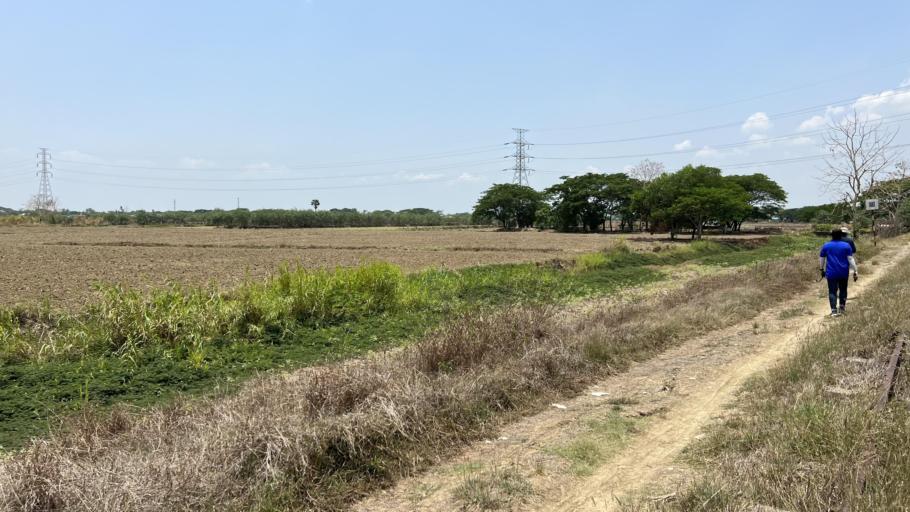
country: MM
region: Yangon
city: Yangon
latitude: 16.8836
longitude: 95.9985
